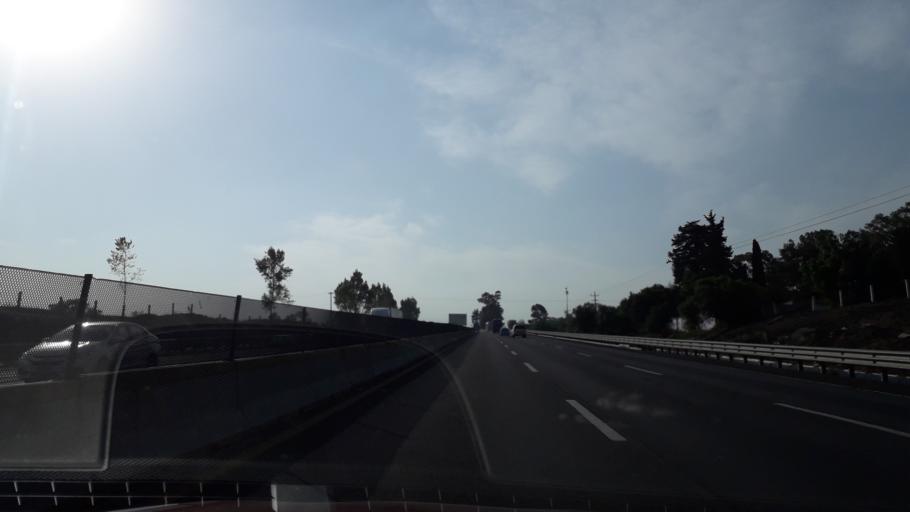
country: MX
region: Puebla
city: San Matias Tlalancaleca
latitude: 19.3185
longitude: -98.5102
